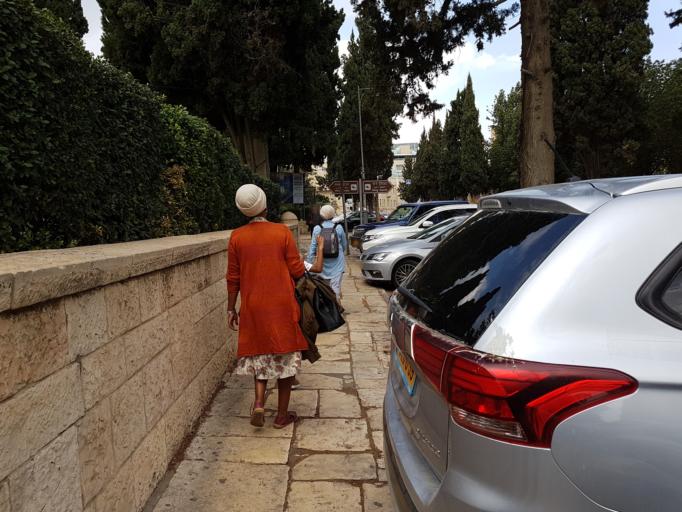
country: IL
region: Jerusalem
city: Jerusalem
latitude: 31.7741
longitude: 35.2220
